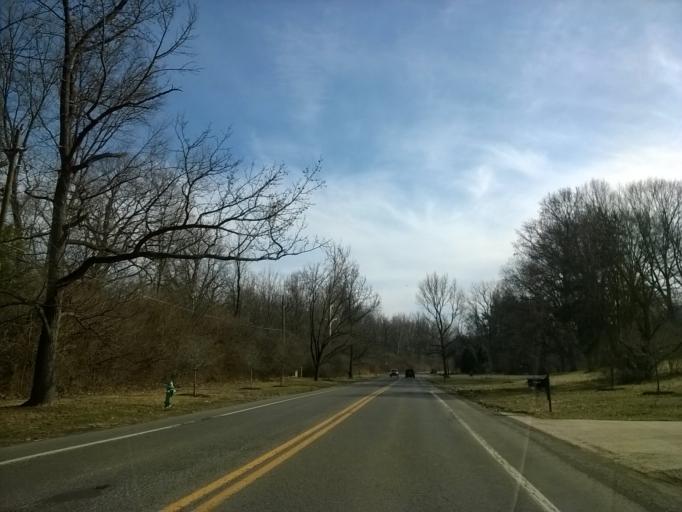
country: US
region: Indiana
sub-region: Marion County
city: Speedway
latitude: 39.8400
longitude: -86.2118
